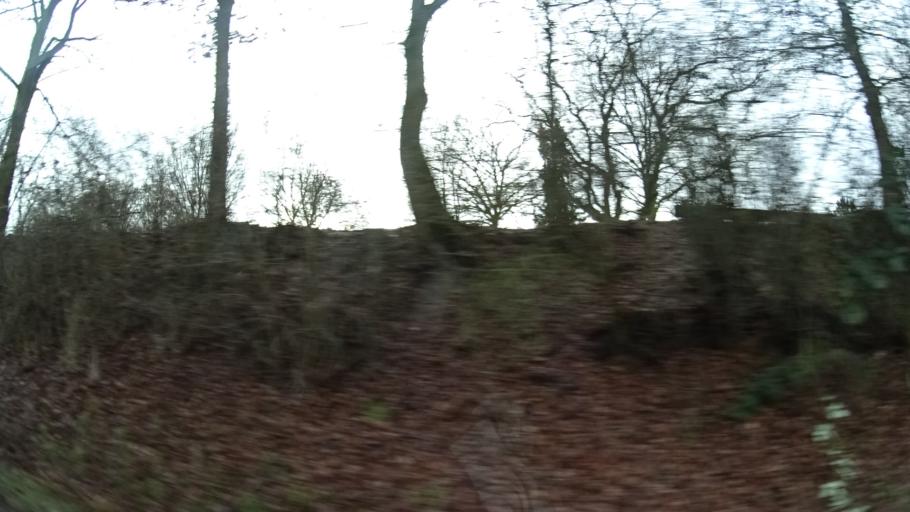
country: DE
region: Hesse
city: Tann
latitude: 50.6299
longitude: 10.0188
